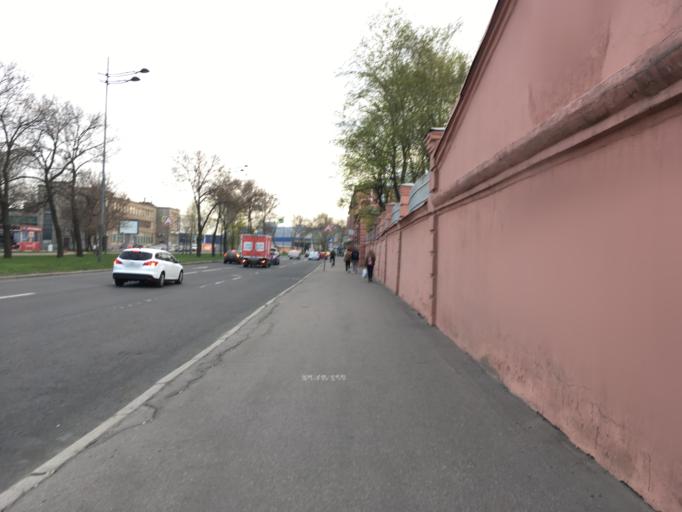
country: RU
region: St.-Petersburg
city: Centralniy
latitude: 59.9004
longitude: 30.3384
